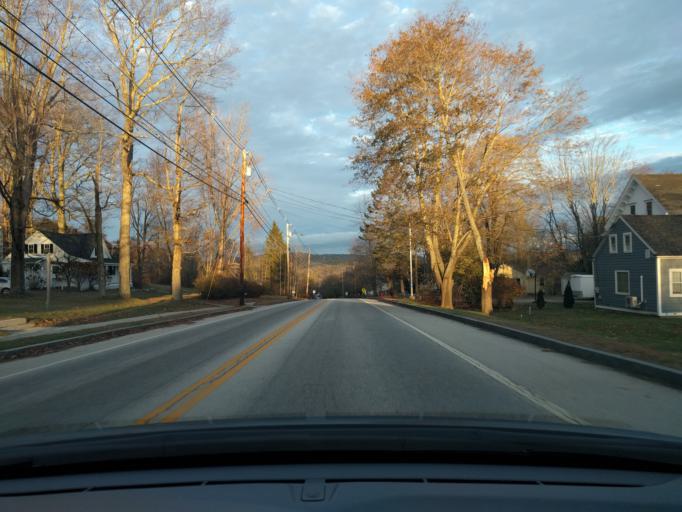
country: US
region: Maine
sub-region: Waldo County
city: Winterport
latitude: 44.6308
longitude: -68.8554
